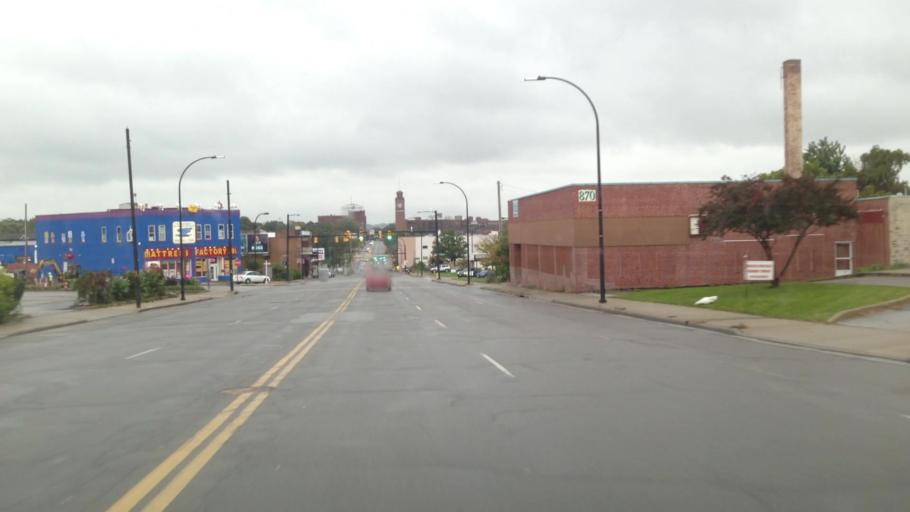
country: US
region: Ohio
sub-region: Summit County
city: Akron
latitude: 41.0733
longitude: -81.4918
